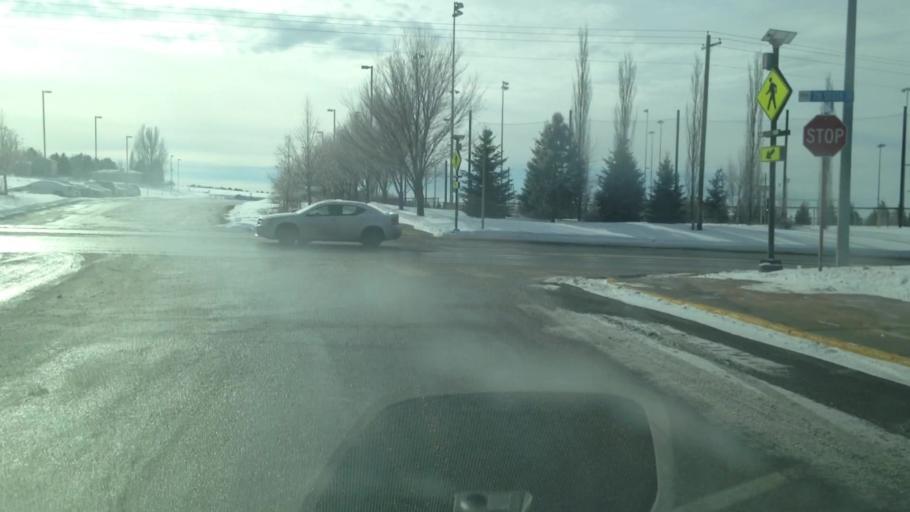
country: US
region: Idaho
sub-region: Madison County
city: Rexburg
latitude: 43.8118
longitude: -111.7839
